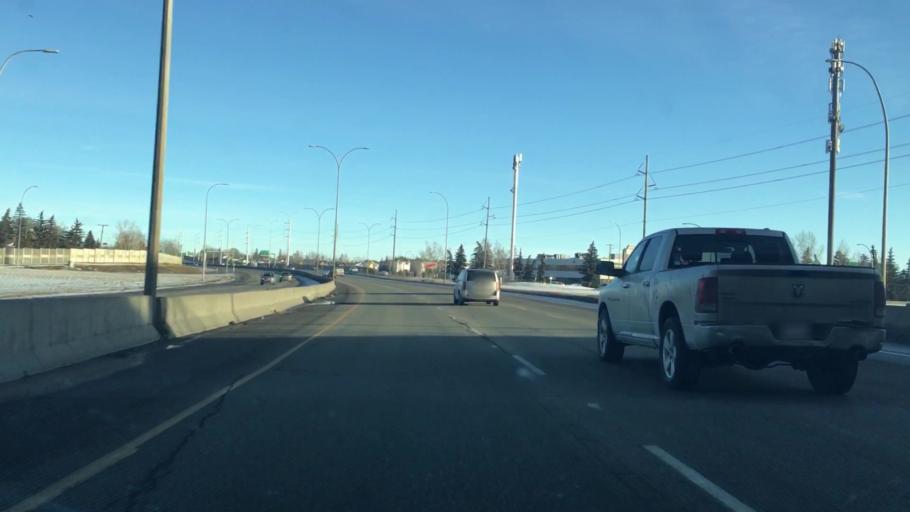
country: CA
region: Alberta
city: Calgary
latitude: 50.9804
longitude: -114.0153
